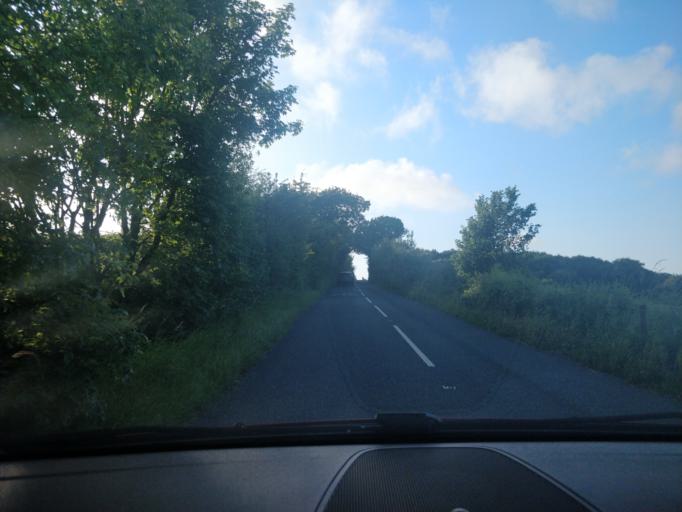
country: GB
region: England
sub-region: Lancashire
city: Skelmersdale
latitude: 53.5562
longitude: -2.7462
